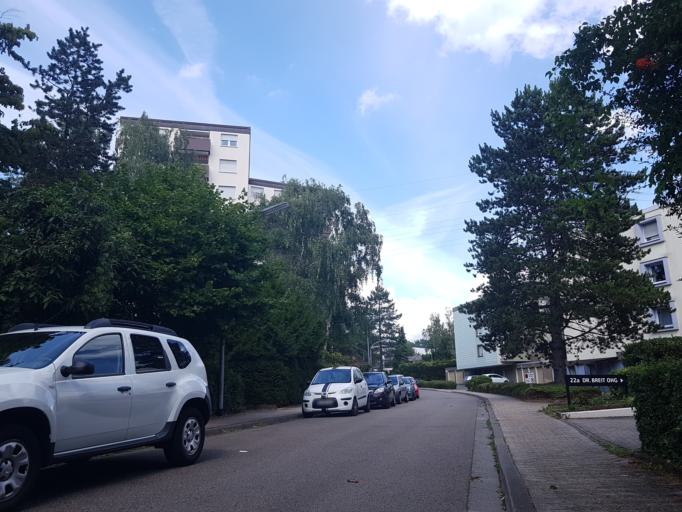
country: DE
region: Saarland
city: Saarbrucken
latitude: 49.2532
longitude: 6.9931
